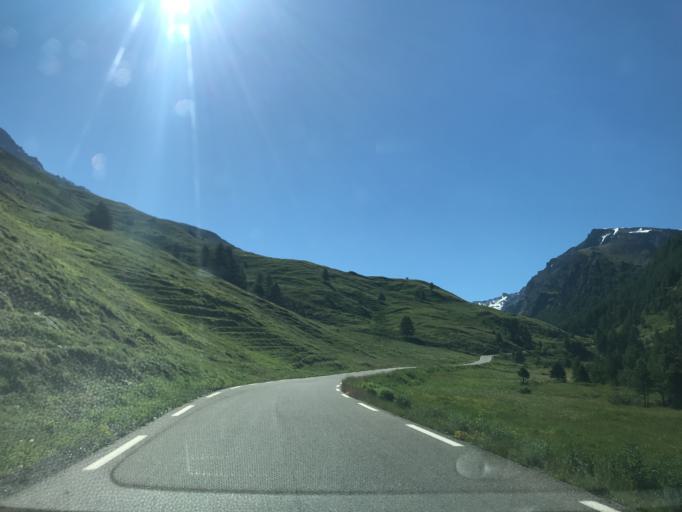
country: IT
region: Piedmont
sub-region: Provincia di Cuneo
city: Pontechianale
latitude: 44.7125
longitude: 6.9194
